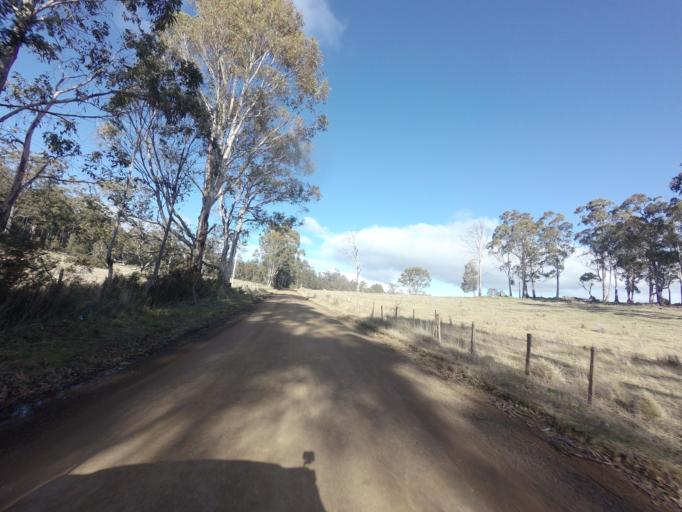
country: AU
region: Tasmania
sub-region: Derwent Valley
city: New Norfolk
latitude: -42.7115
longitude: 147.0294
